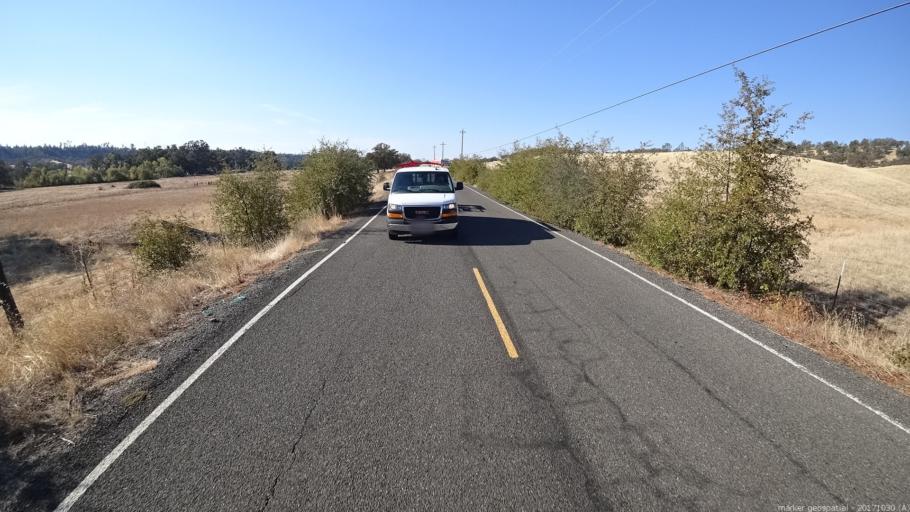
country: US
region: California
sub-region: Shasta County
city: Bella Vista
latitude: 40.6273
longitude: -122.1050
